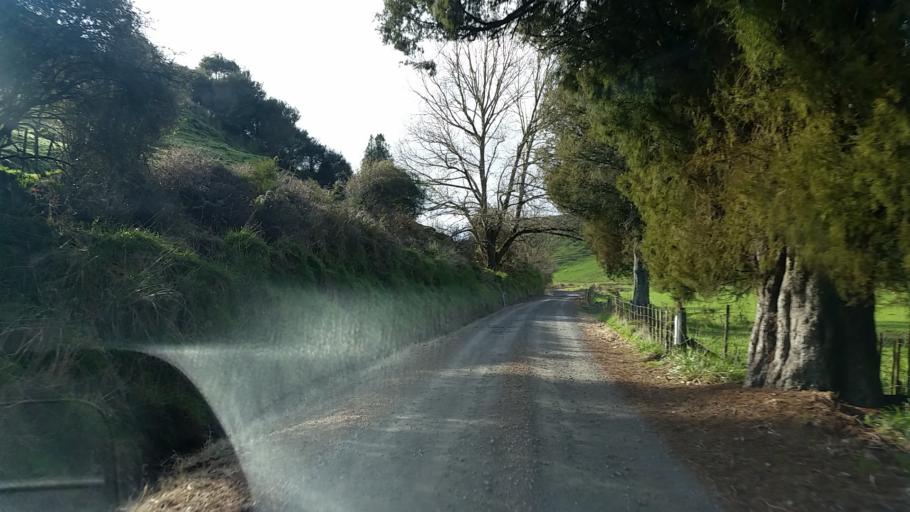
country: NZ
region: Taranaki
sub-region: South Taranaki District
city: Eltham
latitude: -39.2556
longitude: 174.5269
